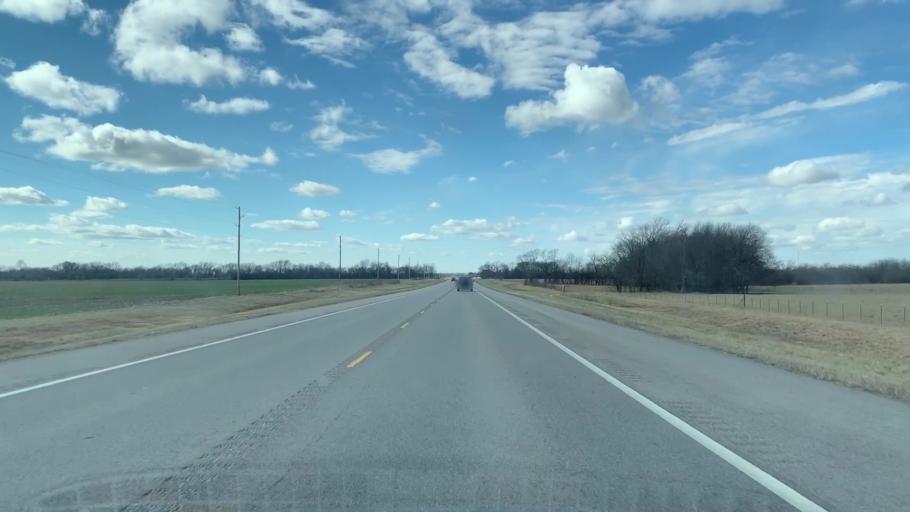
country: US
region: Kansas
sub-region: Labette County
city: Oswego
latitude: 37.3401
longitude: -95.0323
